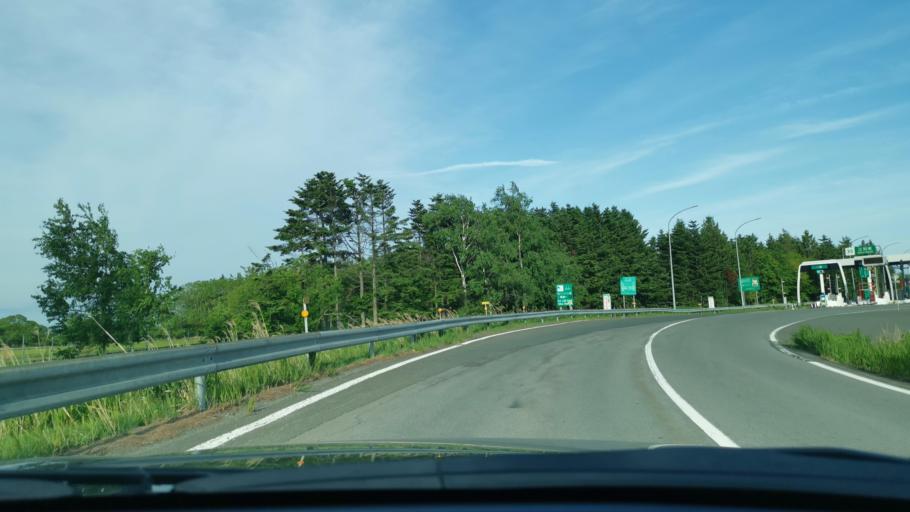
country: JP
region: Hokkaido
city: Ebetsu
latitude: 43.1074
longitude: 141.5972
